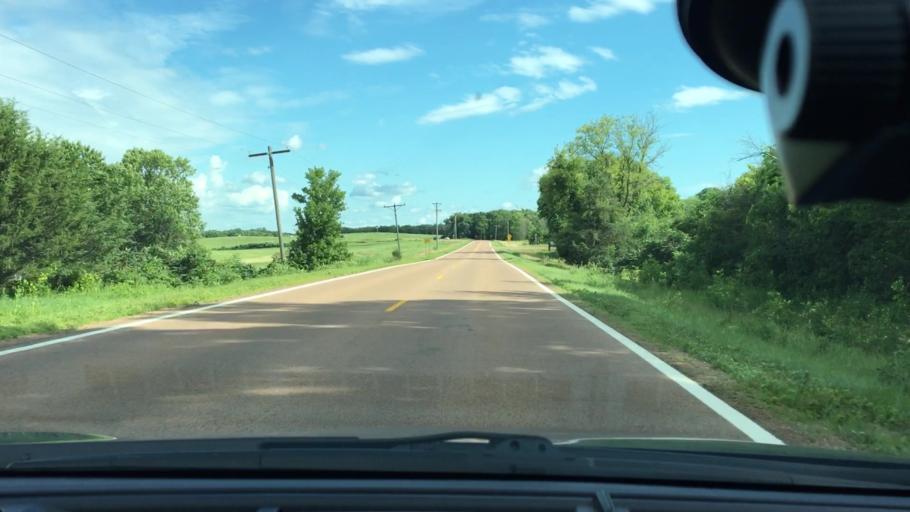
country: US
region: Minnesota
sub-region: Hennepin County
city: Saint Bonifacius
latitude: 44.8854
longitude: -93.7039
